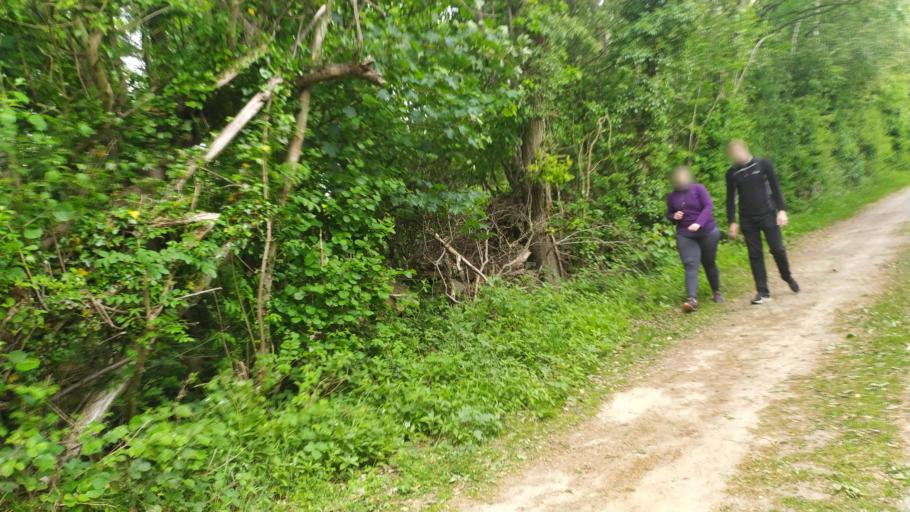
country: GB
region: England
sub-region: City and Borough of Leeds
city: Thorner
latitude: 53.8620
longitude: -1.3951
